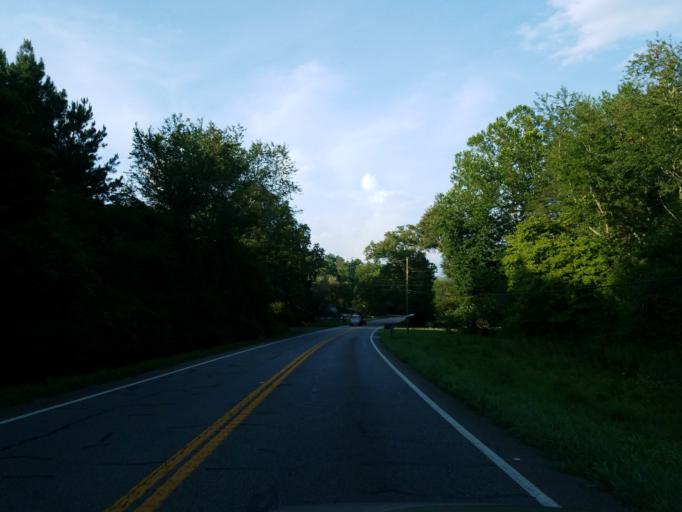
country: US
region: Georgia
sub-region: Pickens County
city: Jasper
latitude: 34.5137
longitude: -84.5444
